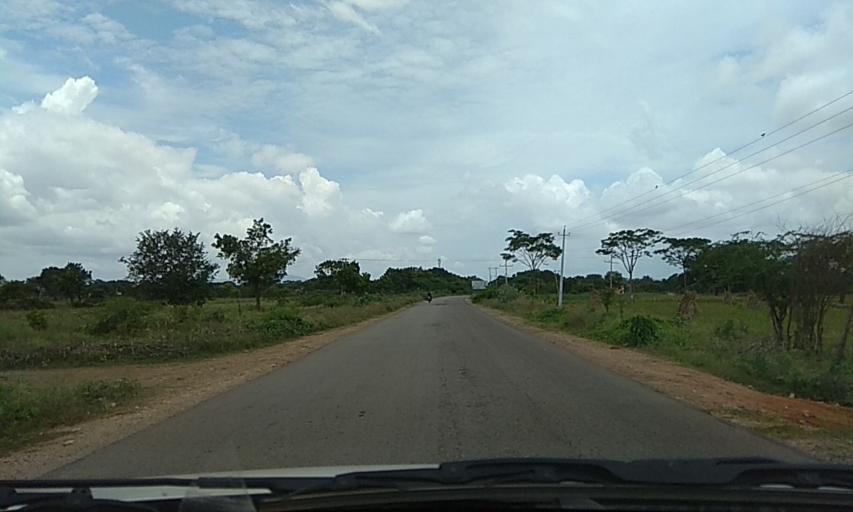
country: IN
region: Karnataka
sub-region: Chamrajnagar
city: Gundlupet
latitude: 11.8114
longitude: 76.7428
